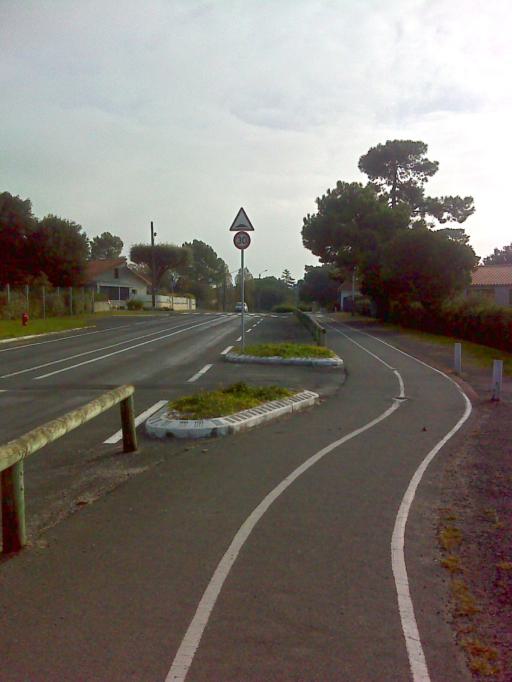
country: FR
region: Poitou-Charentes
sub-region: Departement de la Charente-Maritime
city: Saint-Palais-sur-Mer
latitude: 45.6470
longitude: -1.1073
